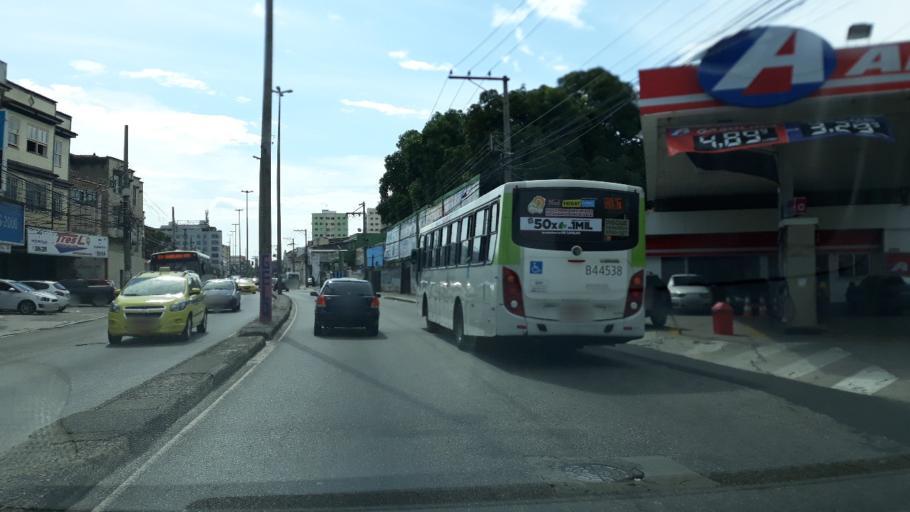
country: BR
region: Rio de Janeiro
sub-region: Duque De Caxias
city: Duque de Caxias
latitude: -22.8851
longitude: -43.3108
